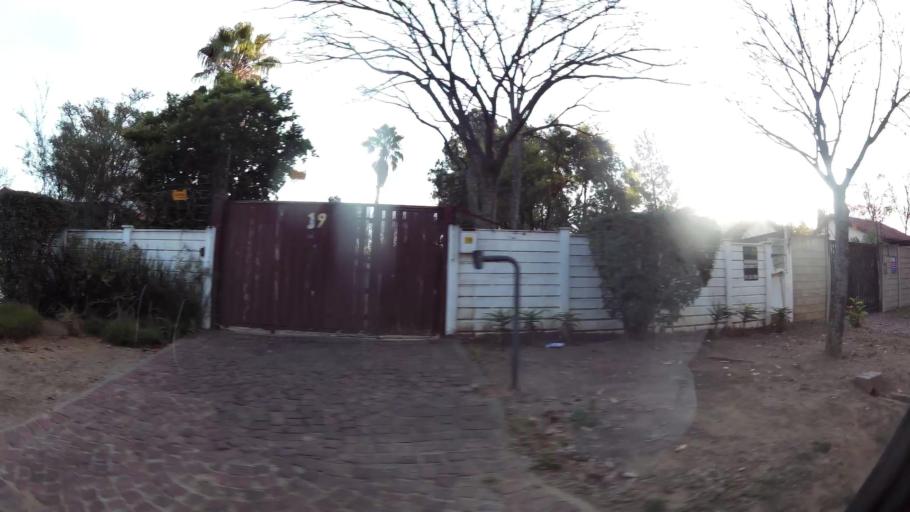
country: ZA
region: Gauteng
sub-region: City of Johannesburg Metropolitan Municipality
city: Diepsloot
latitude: -26.0393
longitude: 27.9819
